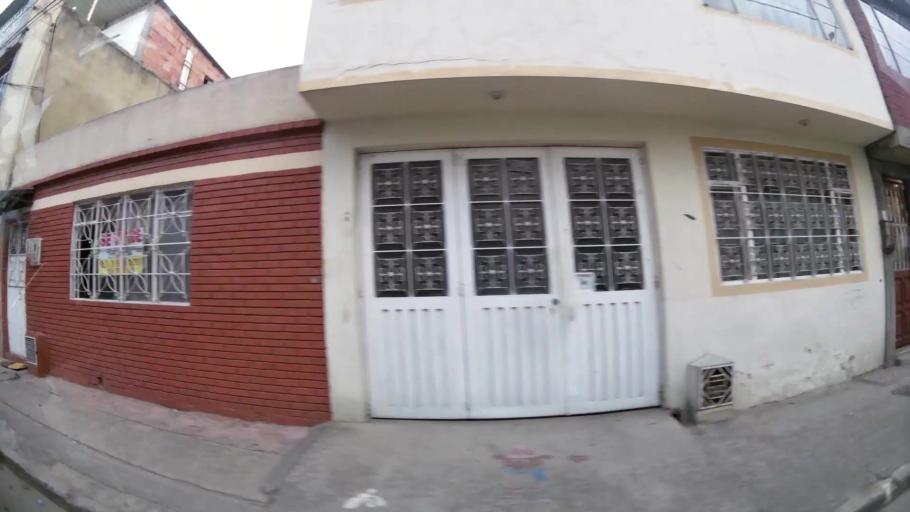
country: CO
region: Cundinamarca
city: Soacha
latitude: 4.6192
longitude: -74.1643
